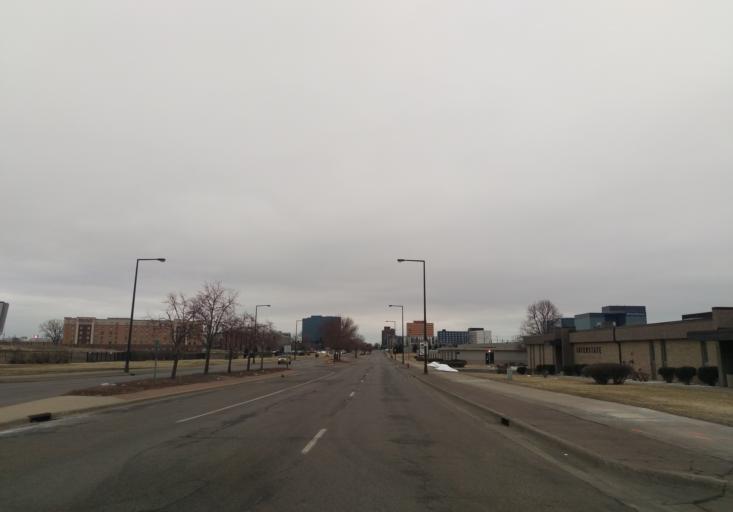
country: US
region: Minnesota
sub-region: Hennepin County
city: Richfield
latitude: 44.8587
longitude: -93.2361
